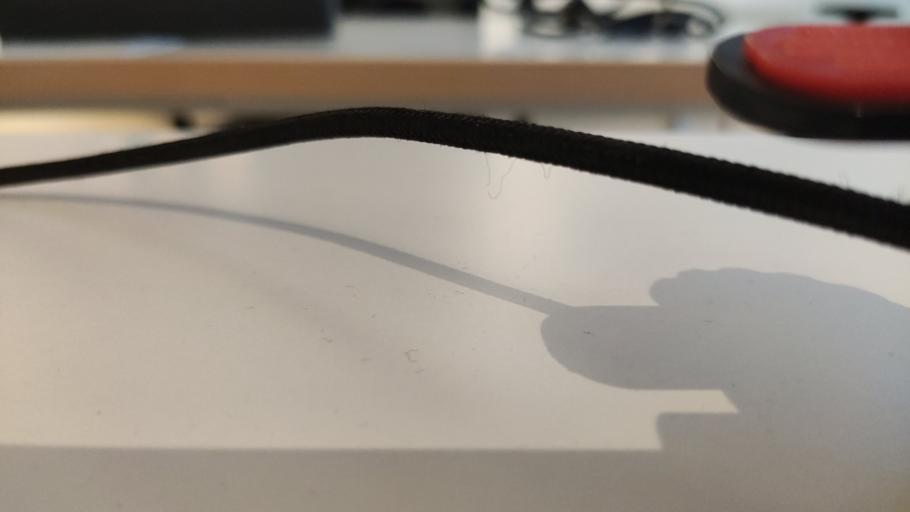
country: RU
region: Moskovskaya
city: Sychevo
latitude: 55.8183
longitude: 36.3024
